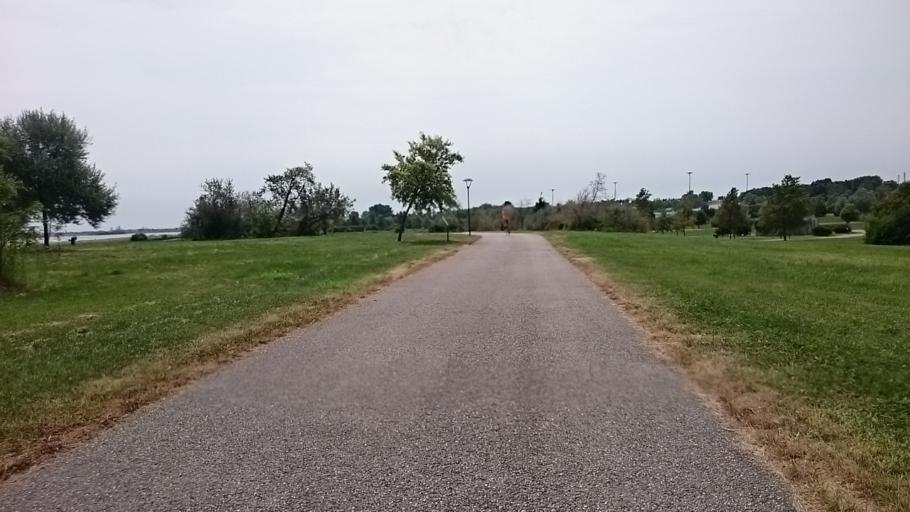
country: IT
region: Veneto
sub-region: Provincia di Venezia
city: Campalto
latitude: 45.4736
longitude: 12.2770
